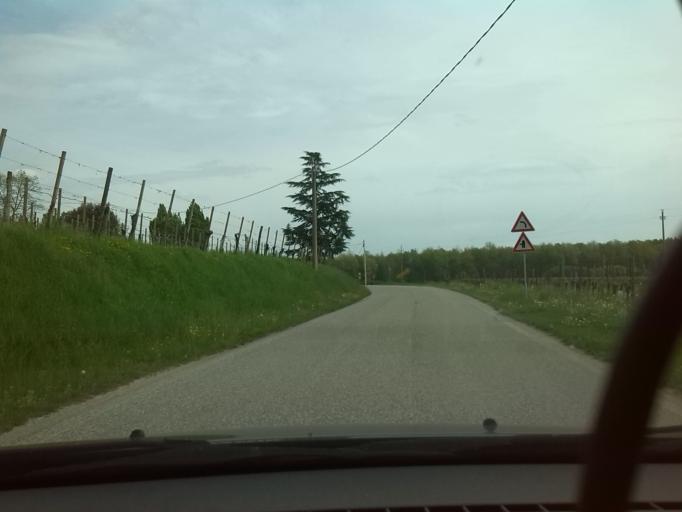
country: SI
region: Brda
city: Dobrovo
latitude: 45.9744
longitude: 13.5025
